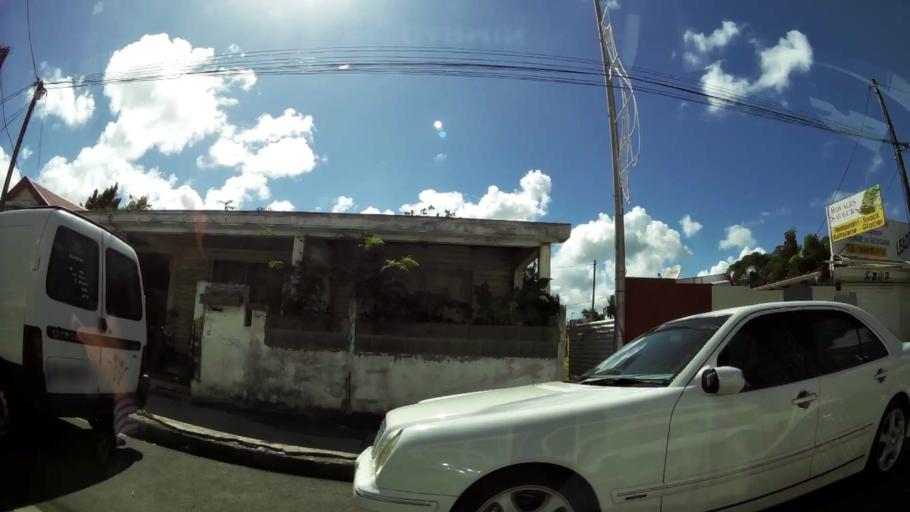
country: GP
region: Guadeloupe
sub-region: Guadeloupe
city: Le Moule
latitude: 16.3306
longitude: -61.3452
